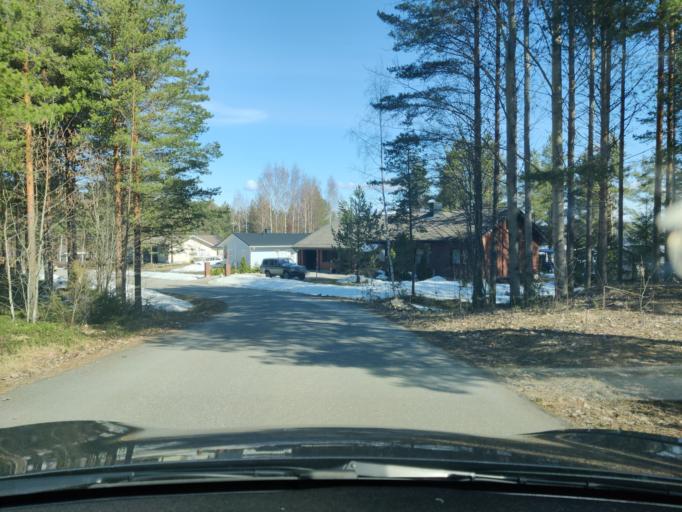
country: FI
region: Northern Savo
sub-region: Kuopio
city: Vehmersalmi
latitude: 62.7716
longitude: 27.9866
